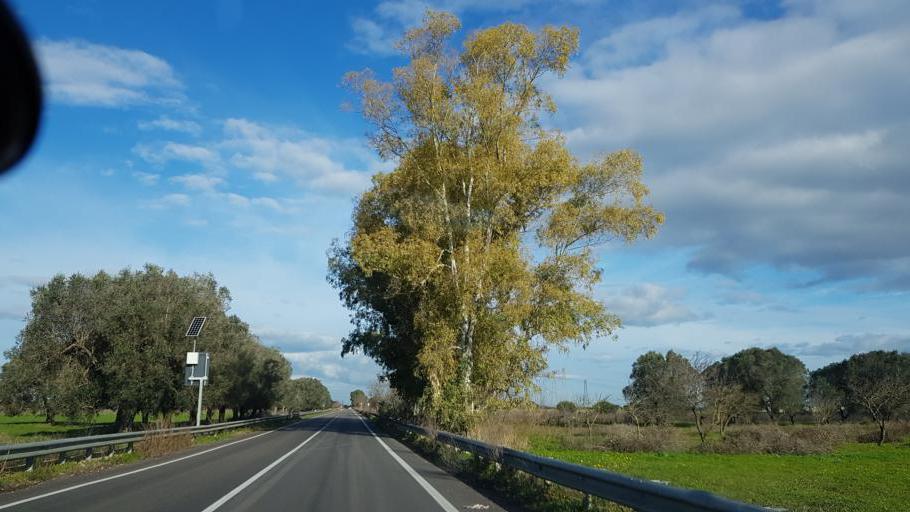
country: IT
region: Apulia
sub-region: Provincia di Brindisi
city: Tuturano
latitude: 40.5530
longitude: 17.9748
